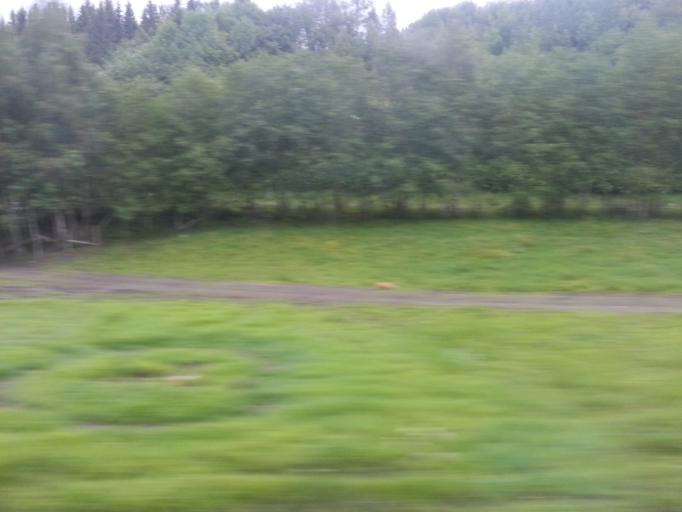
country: NO
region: Sor-Trondelag
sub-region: Melhus
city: Lundamo
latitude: 63.1254
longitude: 10.2424
